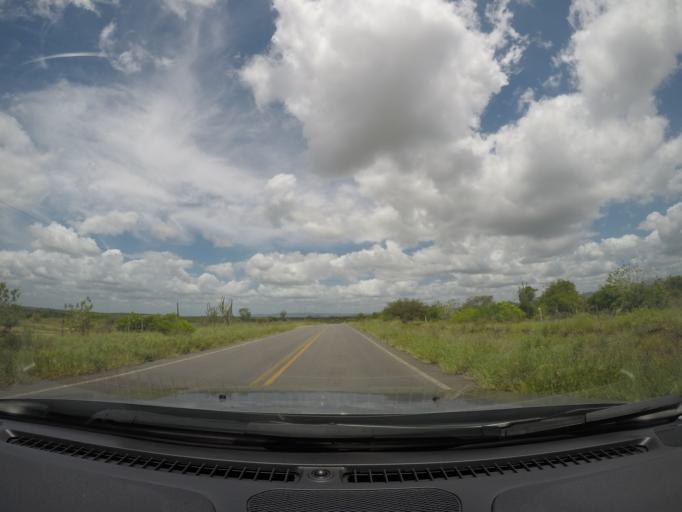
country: BR
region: Bahia
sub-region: Ipira
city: Ipira
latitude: -12.2898
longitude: -39.8734
